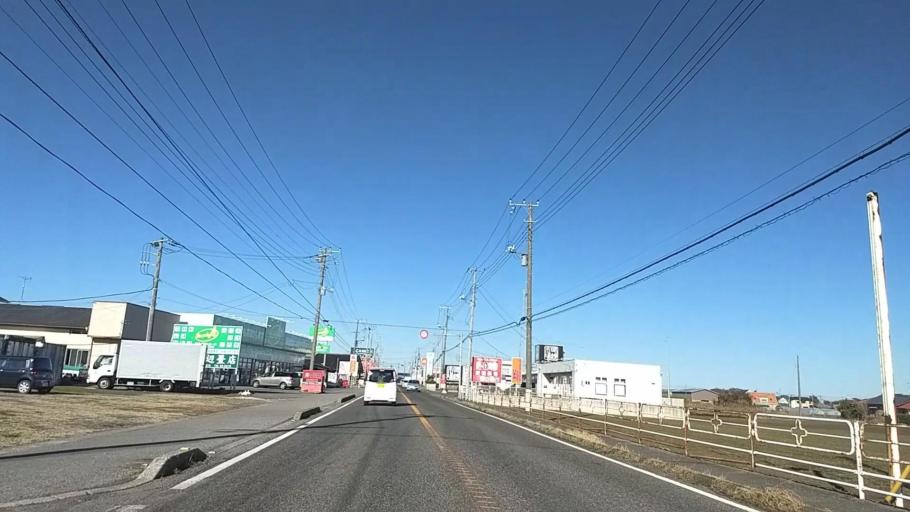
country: JP
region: Chiba
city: Ohara
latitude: 35.2728
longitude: 140.3941
